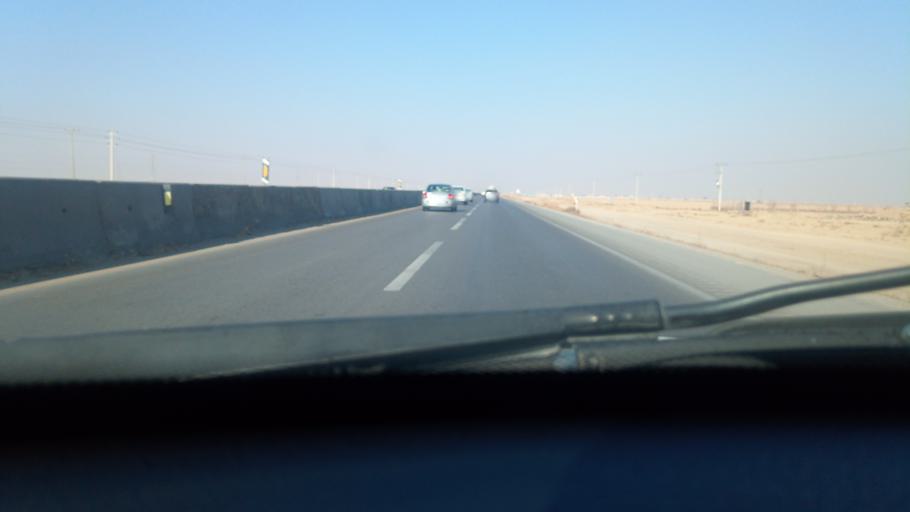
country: IR
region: Razavi Khorasan
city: Chenaran
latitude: 36.7996
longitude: 58.8618
